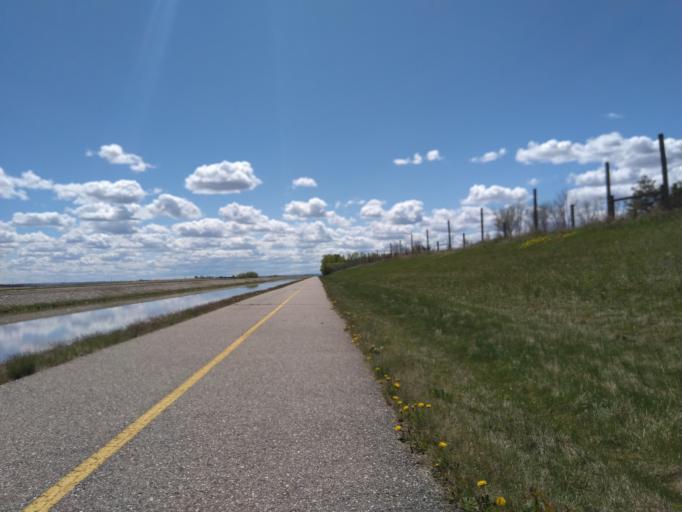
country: CA
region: Alberta
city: Chestermere
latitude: 50.9977
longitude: -113.8602
